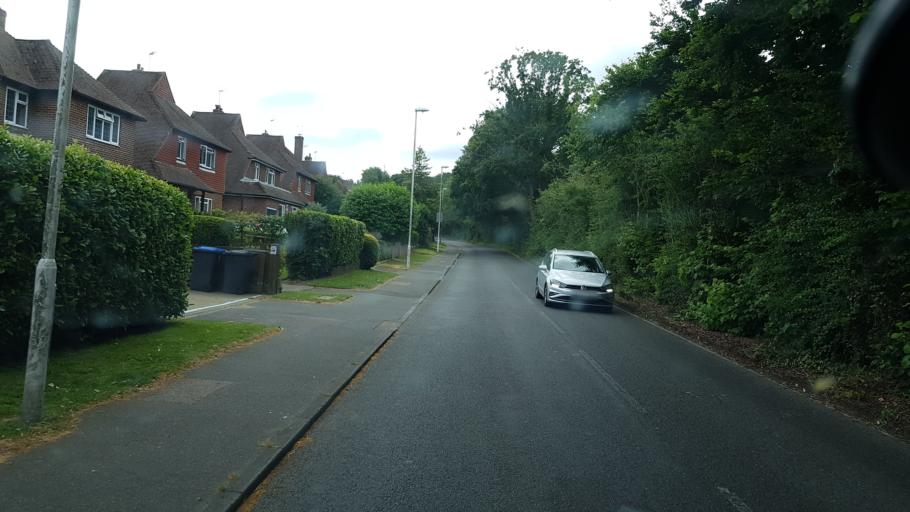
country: GB
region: England
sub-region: Surrey
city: Felbridge
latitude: 51.1318
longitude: -0.0327
